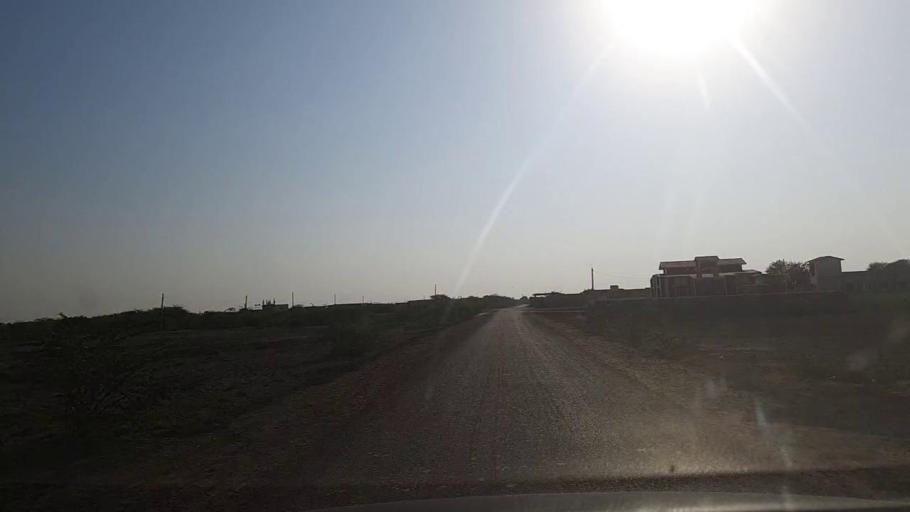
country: PK
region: Sindh
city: Naukot
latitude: 24.9928
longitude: 69.2561
